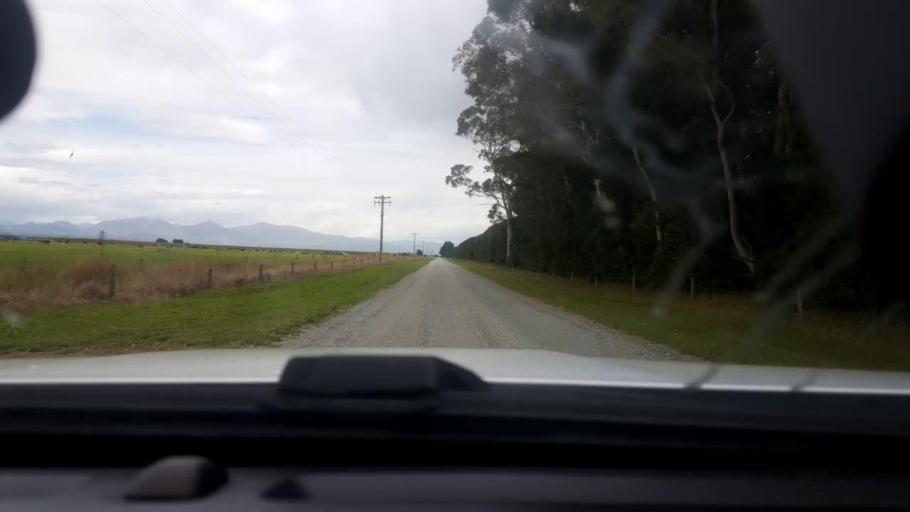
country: NZ
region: Canterbury
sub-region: Timaru District
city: Pleasant Point
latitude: -44.1495
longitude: 171.3930
